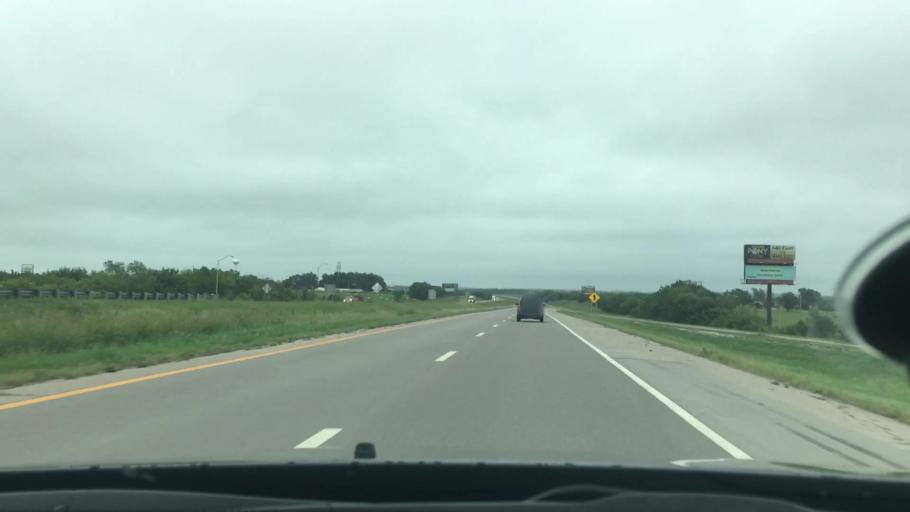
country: US
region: Oklahoma
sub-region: Okfuskee County
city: Okemah
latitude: 35.4222
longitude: -96.2990
